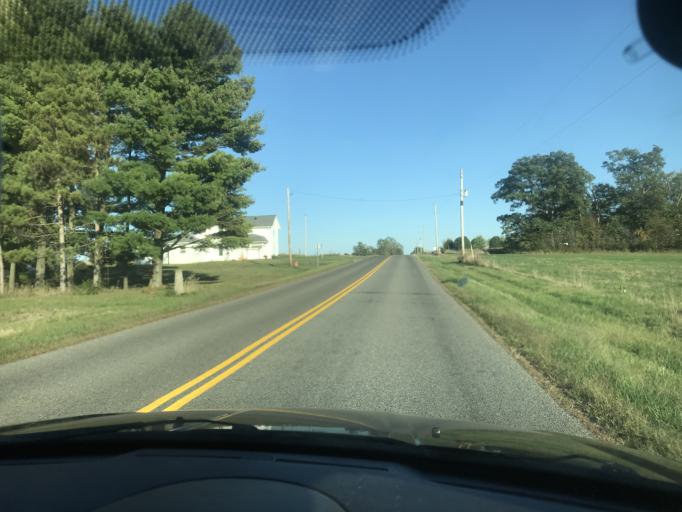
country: US
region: Ohio
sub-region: Logan County
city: De Graff
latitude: 40.3224
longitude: -83.8458
